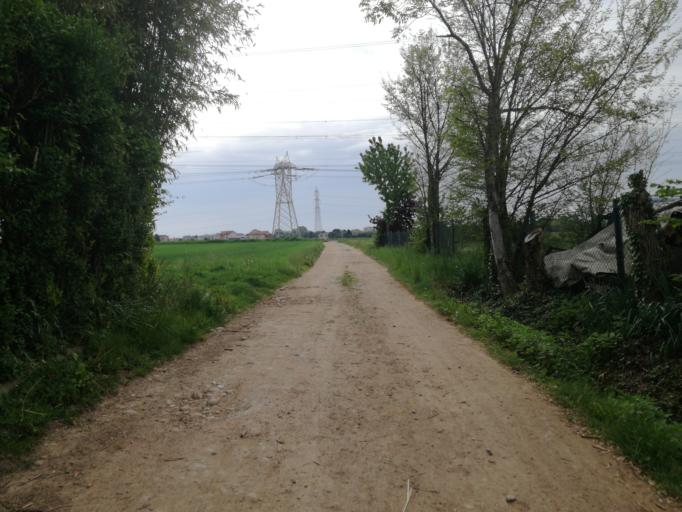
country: IT
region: Lombardy
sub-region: Provincia di Lecco
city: Verderio Superiore
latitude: 45.6537
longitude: 9.4498
